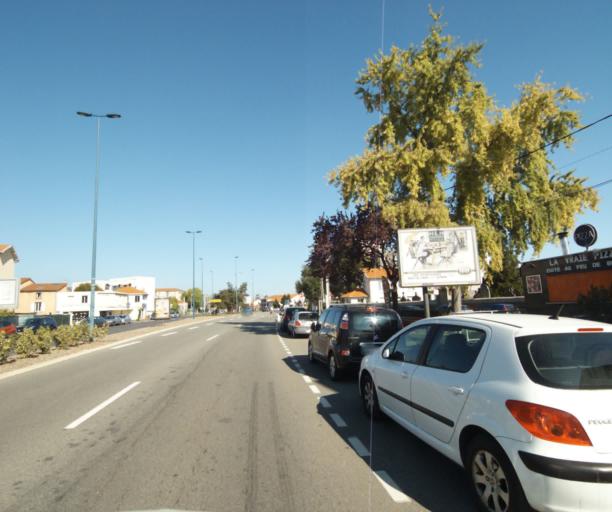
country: FR
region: Auvergne
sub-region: Departement du Puy-de-Dome
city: Clermont-Ferrand
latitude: 45.7908
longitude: 3.1180
